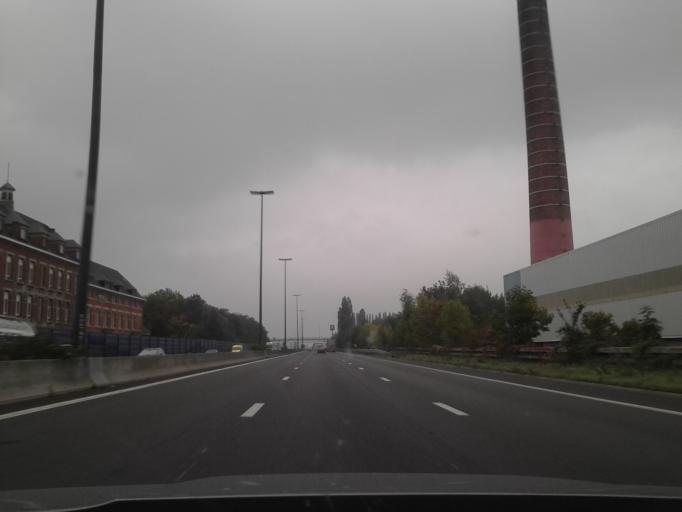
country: BE
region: Wallonia
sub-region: Province du Hainaut
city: Saint-Ghislain
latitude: 50.4525
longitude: 3.8171
